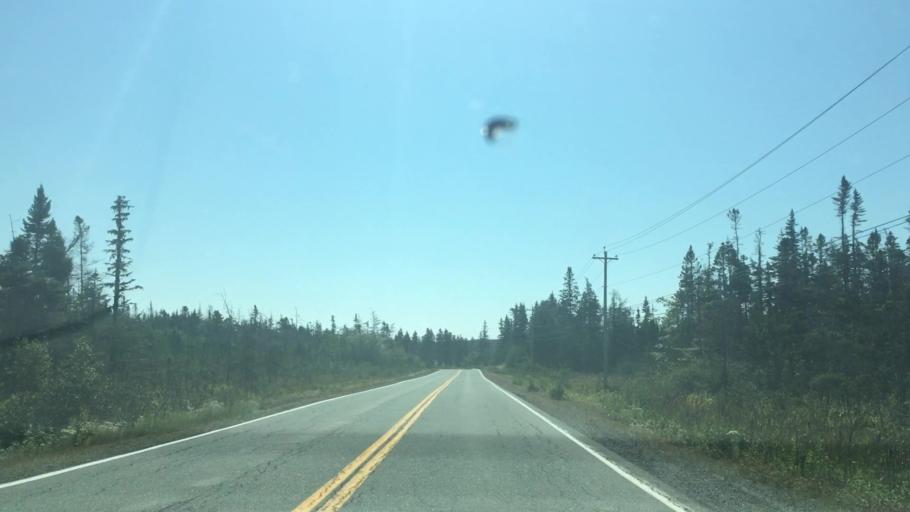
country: CA
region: Nova Scotia
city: Antigonish
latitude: 45.0098
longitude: -62.0907
